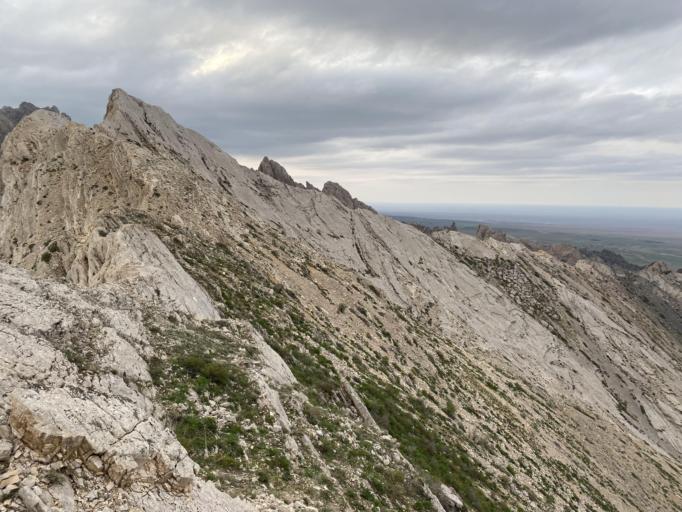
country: KZ
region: Ongtustik Qazaqstan
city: Ashchysay
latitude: 43.7579
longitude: 68.8108
